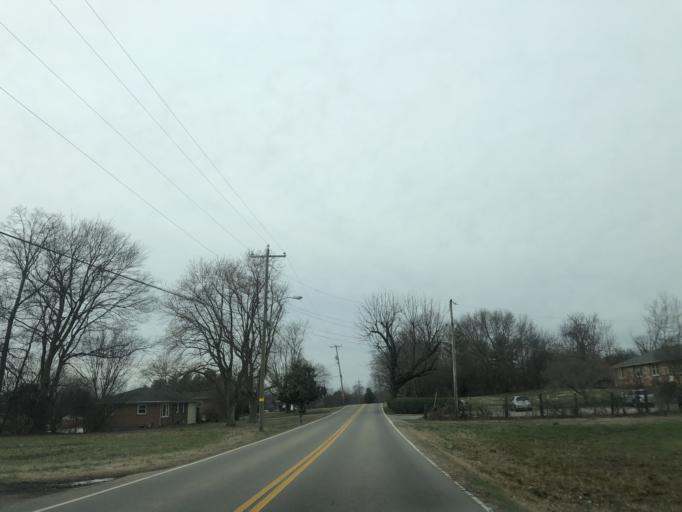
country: US
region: Tennessee
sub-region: Robertson County
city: Ridgetop
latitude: 36.3956
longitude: -86.7852
